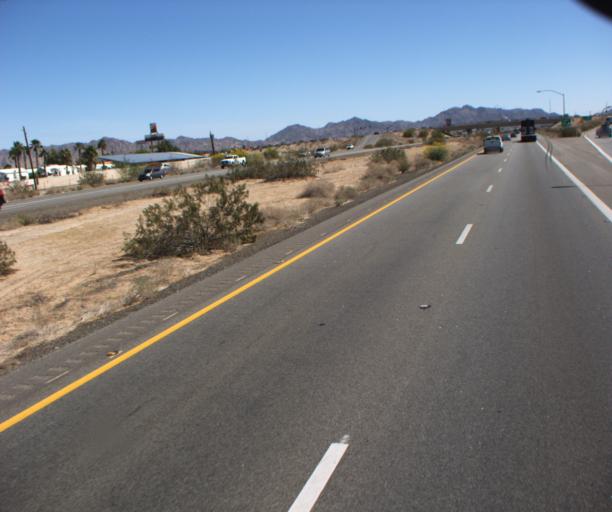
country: US
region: Arizona
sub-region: Yuma County
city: Fortuna Foothills
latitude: 32.6704
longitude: -114.4490
